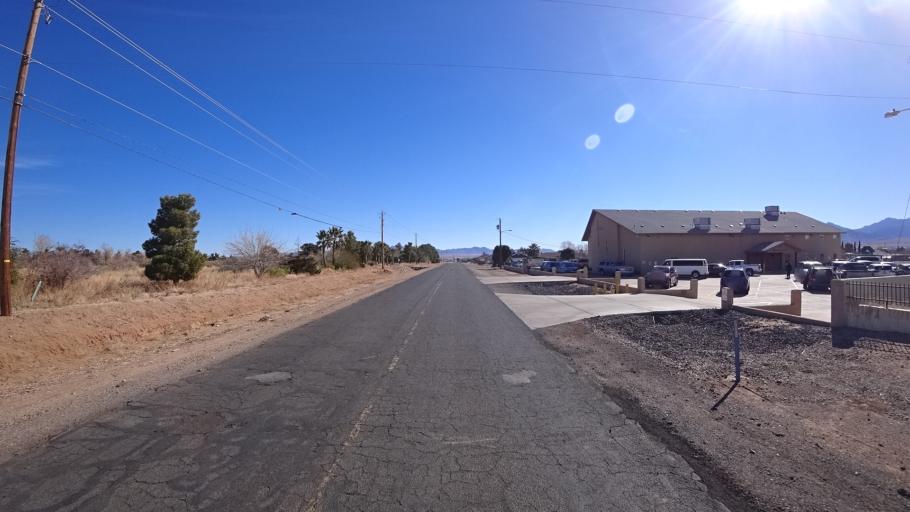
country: US
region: Arizona
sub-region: Mohave County
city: New Kingman-Butler
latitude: 35.2685
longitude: -114.0303
